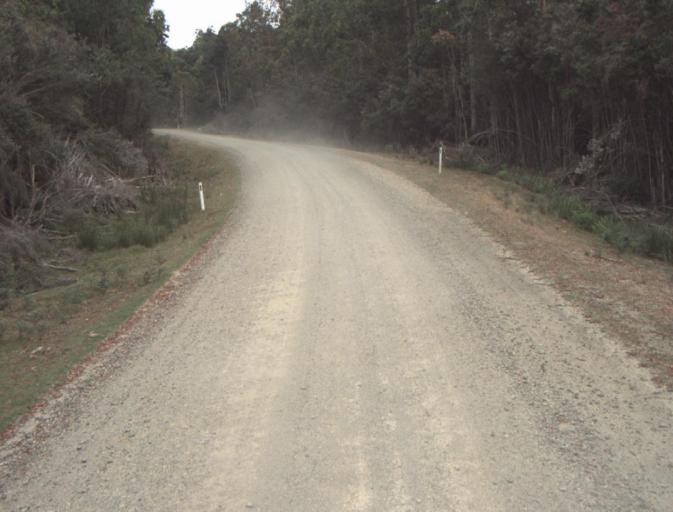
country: AU
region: Tasmania
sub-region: Dorset
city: Scottsdale
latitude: -41.3874
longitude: 147.5056
